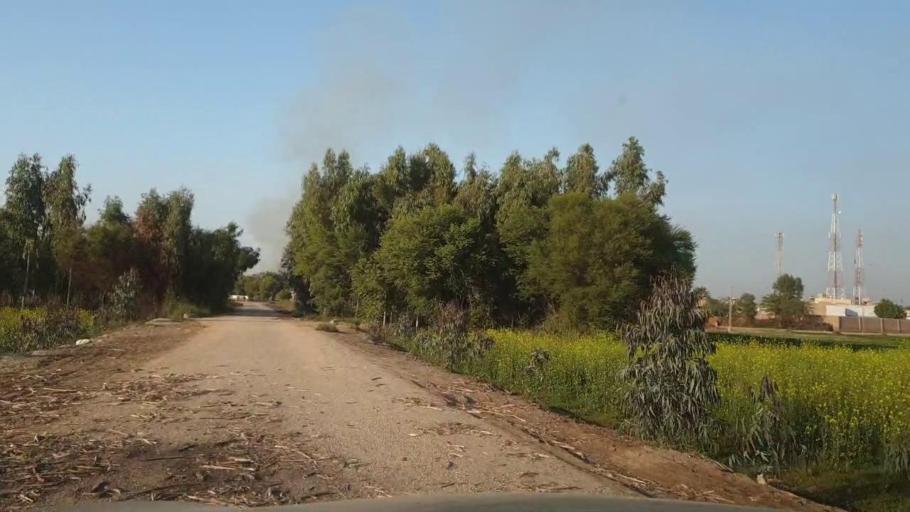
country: PK
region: Sindh
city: Tando Allahyar
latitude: 25.5937
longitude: 68.6908
